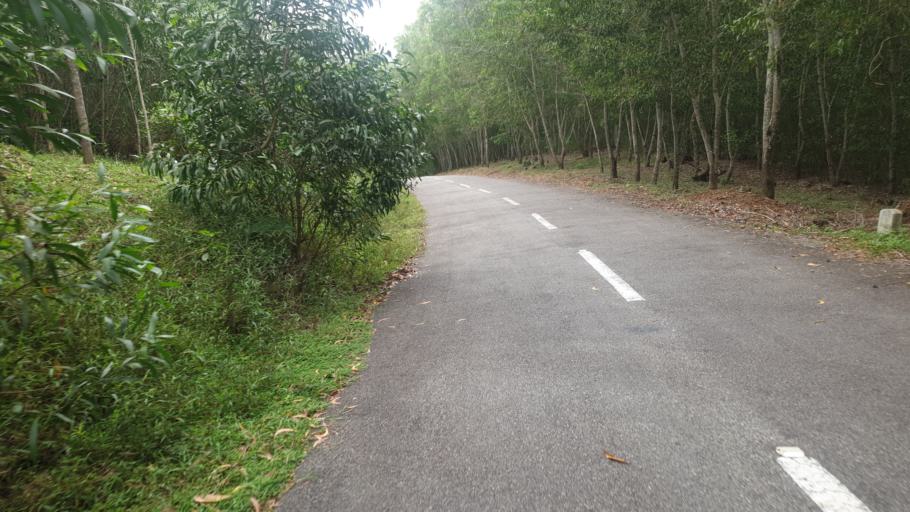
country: IN
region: Kerala
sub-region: Thiruvananthapuram
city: Nedumangad
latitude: 8.6333
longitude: 77.1130
